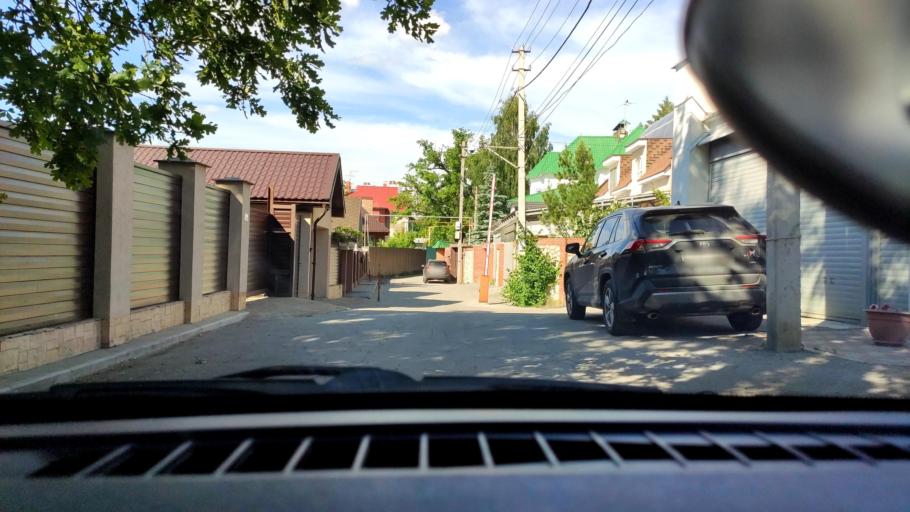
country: RU
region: Samara
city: Samara
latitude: 53.2309
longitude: 50.1749
